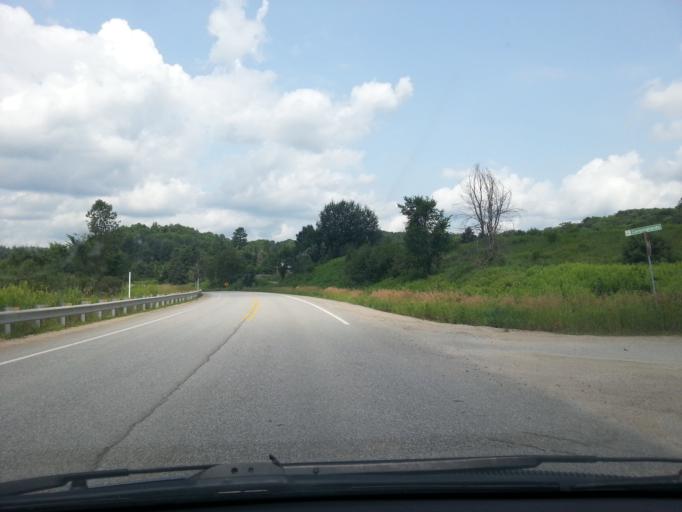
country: CA
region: Quebec
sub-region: Outaouais
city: Val-des-Monts
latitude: 45.6567
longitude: -75.7109
